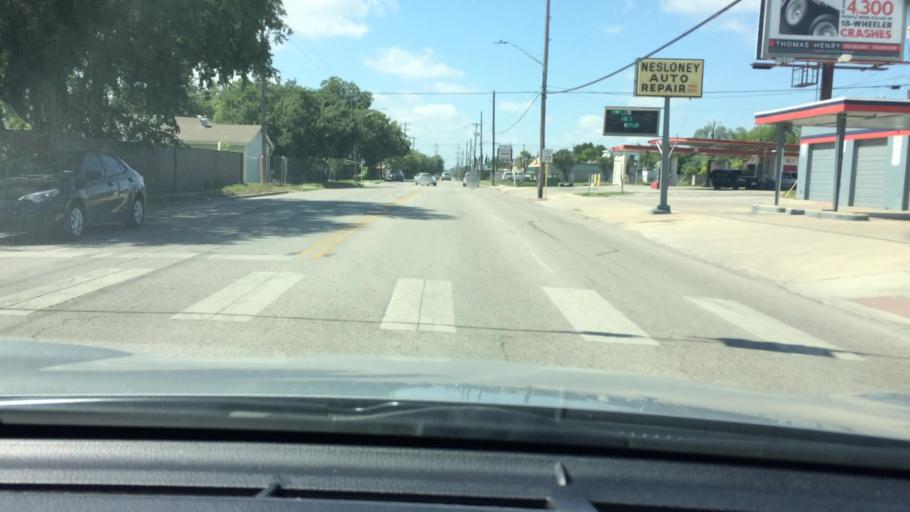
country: US
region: Texas
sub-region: Bexar County
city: Balcones Heights
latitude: 29.4992
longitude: -98.5351
